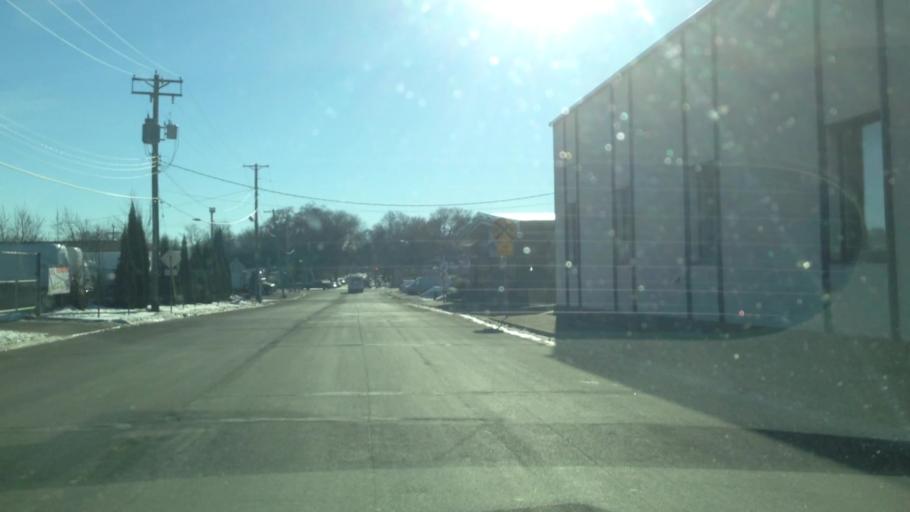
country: US
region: Minnesota
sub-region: Ramsey County
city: Lauderdale
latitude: 44.9933
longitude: -93.2178
